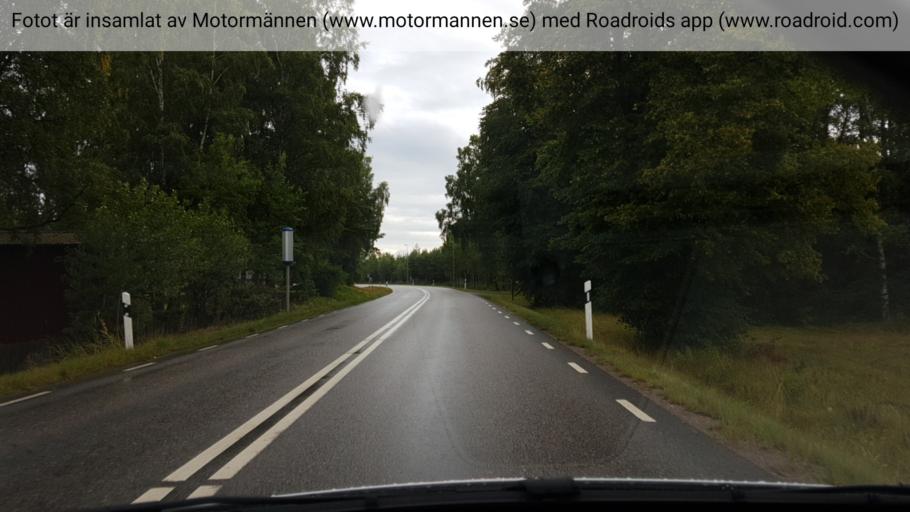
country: SE
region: Vaestra Goetaland
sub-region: Skovde Kommun
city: Stopen
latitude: 58.4368
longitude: 13.9322
